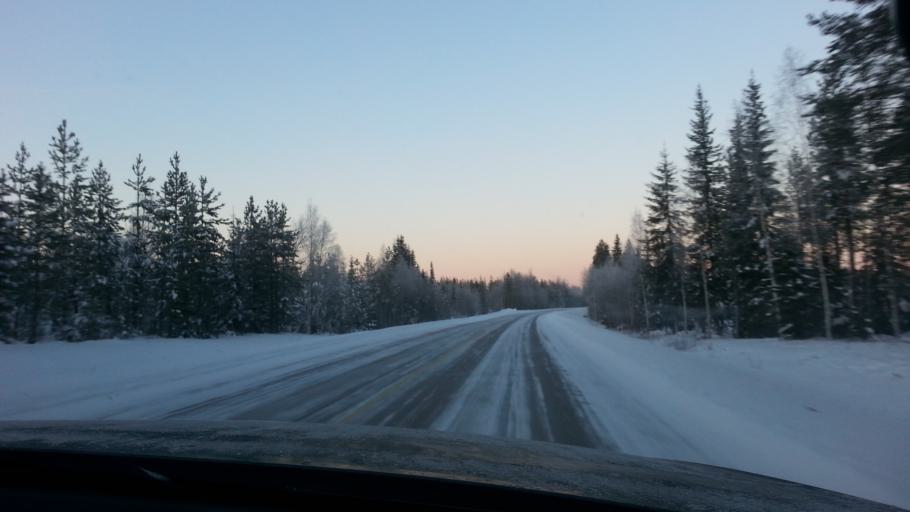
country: FI
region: Lapland
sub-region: Rovaniemi
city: Rovaniemi
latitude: 66.7788
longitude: 25.4504
